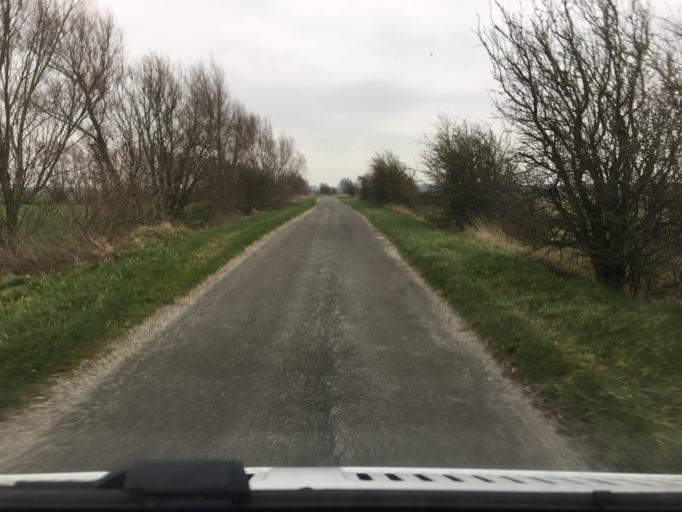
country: FR
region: Picardie
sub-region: Departement de la Somme
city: Pende
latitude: 50.1914
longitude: 1.5462
